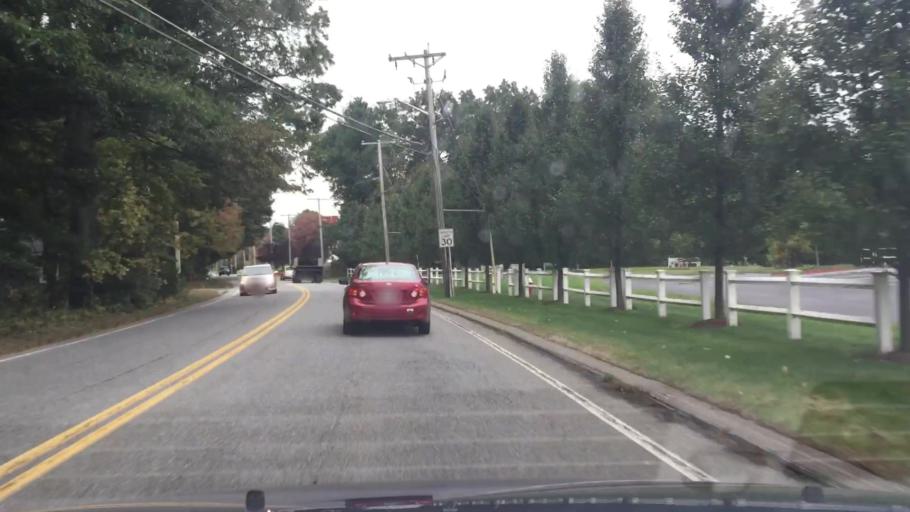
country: US
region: Massachusetts
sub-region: Middlesex County
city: Tyngsboro
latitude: 42.6857
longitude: -71.3730
